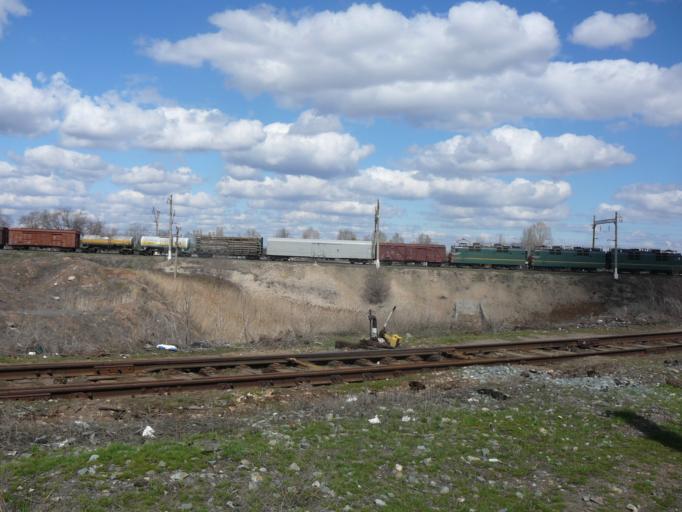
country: RU
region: Saratov
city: Privolzhskiy
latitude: 51.4127
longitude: 46.0643
